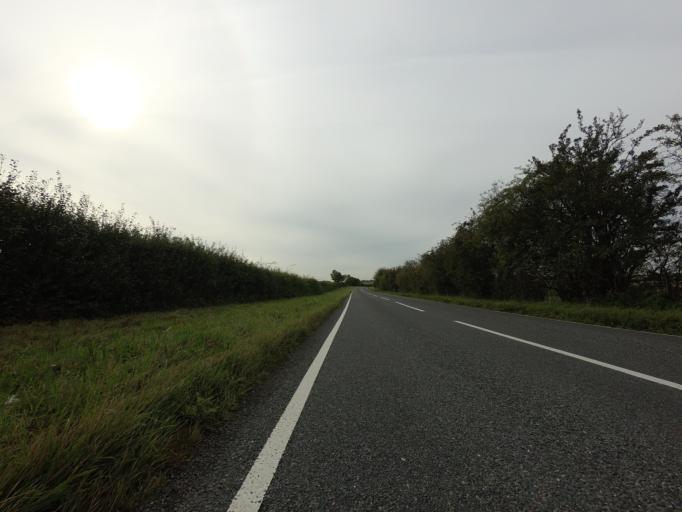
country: GB
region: England
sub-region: Cambridgeshire
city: Melbourn
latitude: 52.0455
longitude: 0.0452
